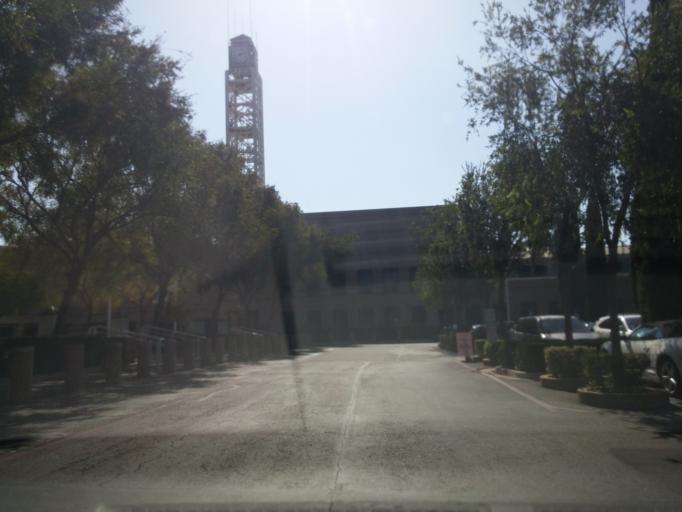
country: US
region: California
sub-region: Orange County
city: Irvine
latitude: 33.6867
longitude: -117.8257
